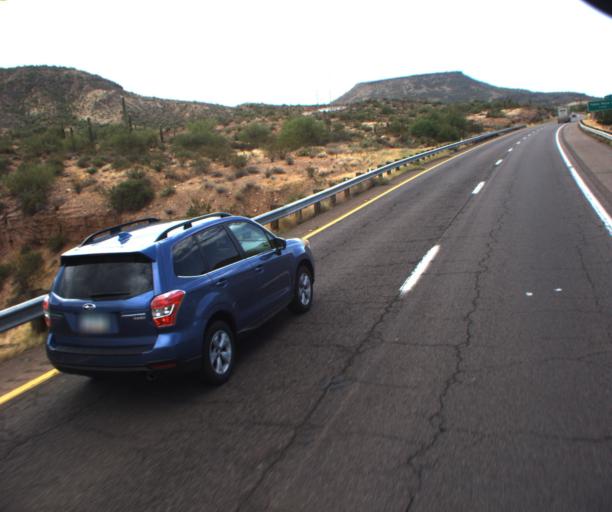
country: US
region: Arizona
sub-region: Maricopa County
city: New River
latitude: 33.9806
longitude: -112.1342
